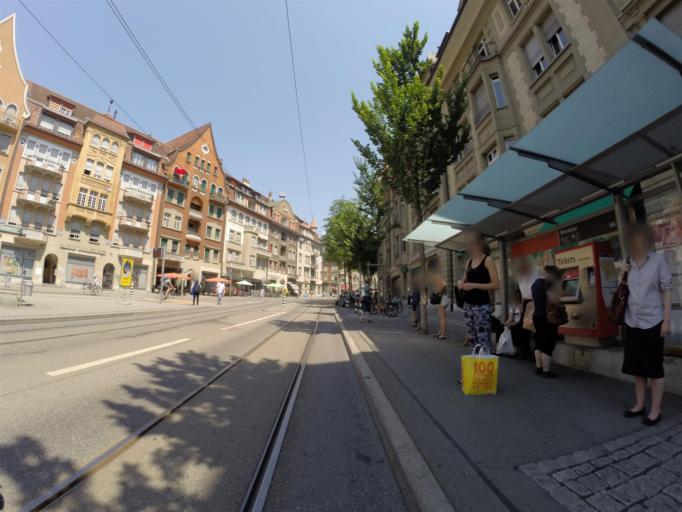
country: CH
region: Bern
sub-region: Bern-Mittelland District
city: Bern
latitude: 46.9435
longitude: 7.4359
